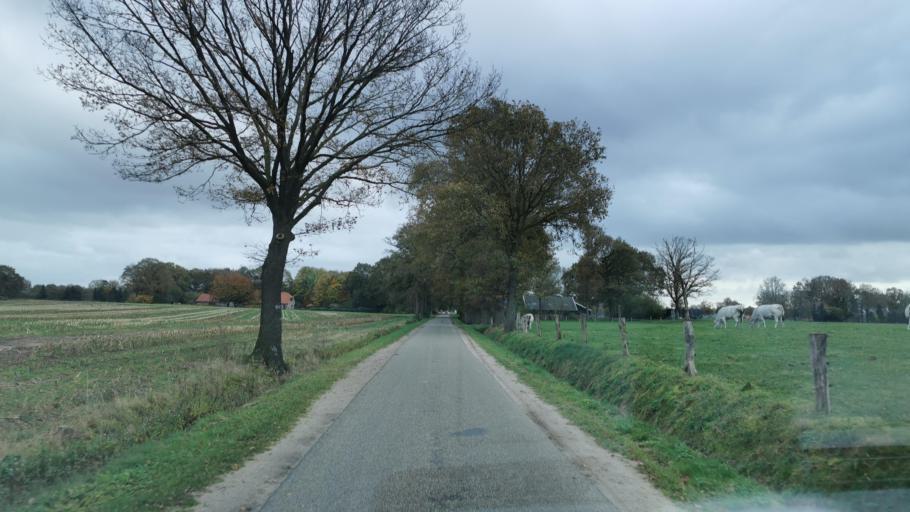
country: NL
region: Overijssel
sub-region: Gemeente Losser
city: Losser
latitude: 52.2515
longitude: 7.0349
